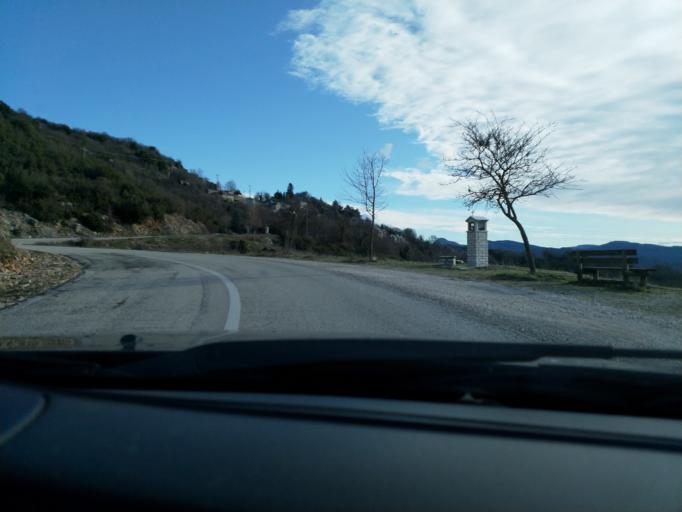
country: GR
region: Epirus
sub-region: Nomos Ioanninon
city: Asprangeloi
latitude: 39.8716
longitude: 20.7439
